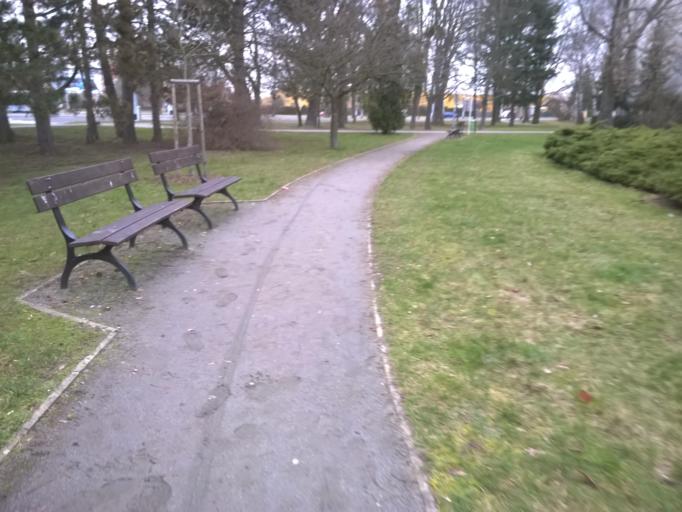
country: CZ
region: Pardubicky
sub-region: Okres Pardubice
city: Pardubice
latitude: 50.0511
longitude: 15.7601
